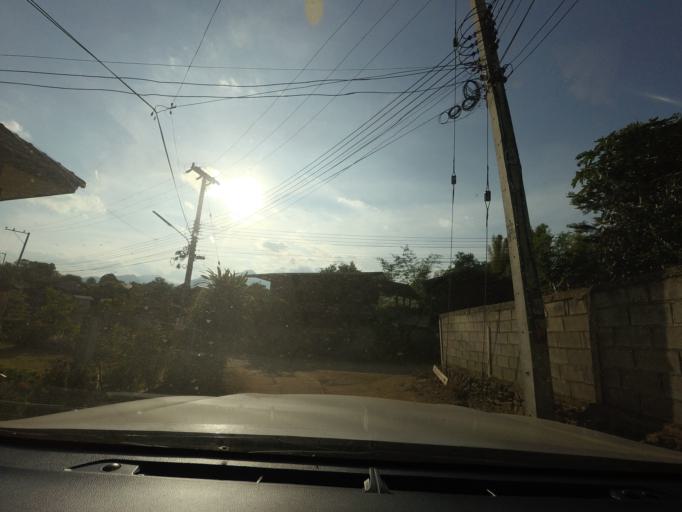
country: TH
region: Mae Hong Son
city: Wiang Nuea
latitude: 19.3986
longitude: 98.4048
